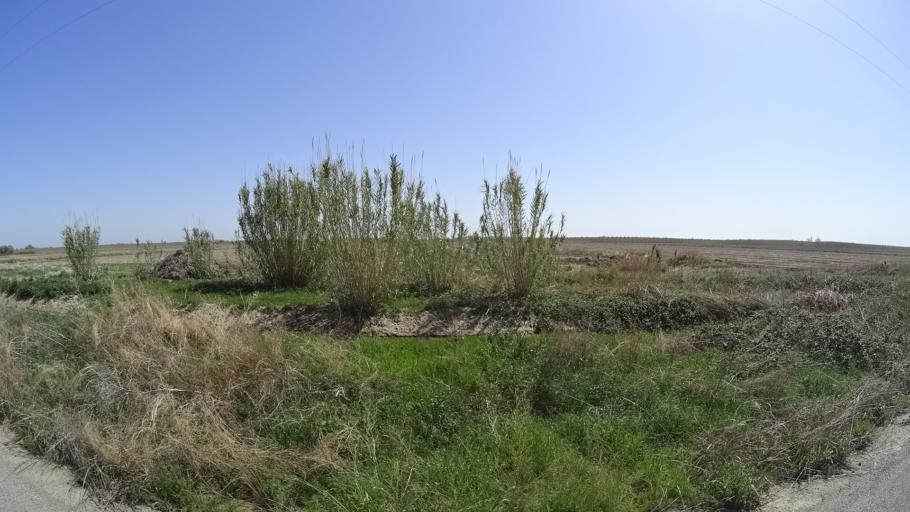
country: US
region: California
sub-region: Glenn County
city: Willows
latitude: 39.5088
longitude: -122.0373
